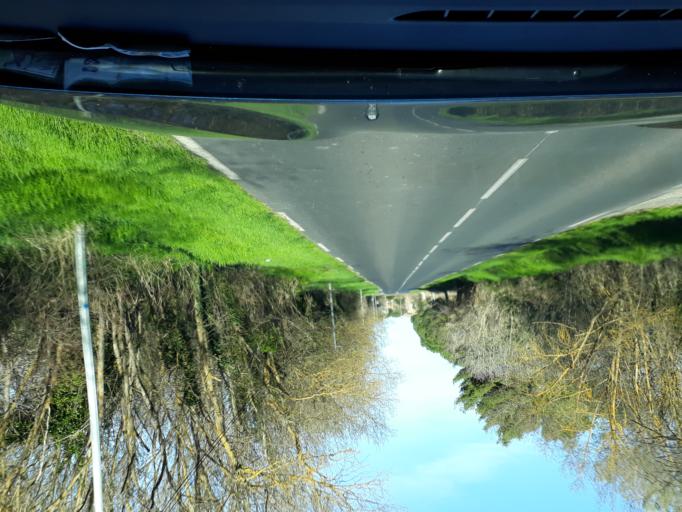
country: FR
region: Languedoc-Roussillon
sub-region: Departement de l'Herault
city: Agde
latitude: 43.3075
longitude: 3.4614
